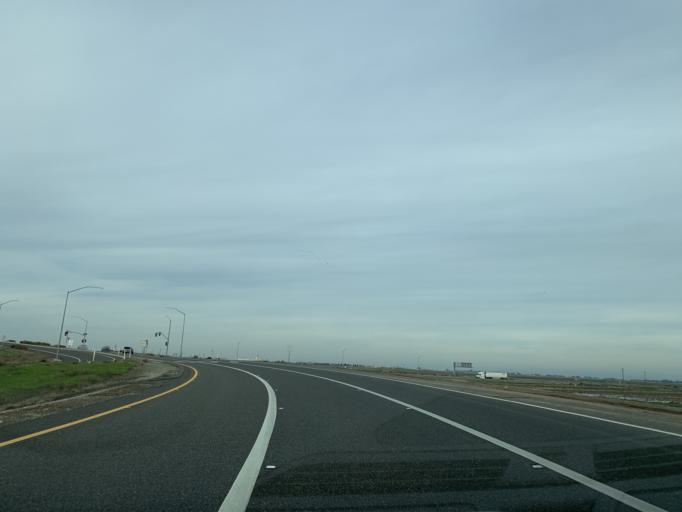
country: US
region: California
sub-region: Sacramento County
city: Elverta
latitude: 38.7487
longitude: -121.5389
